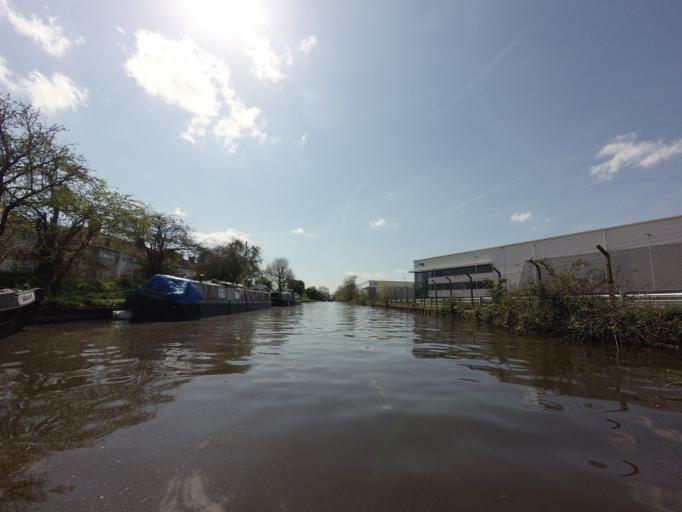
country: GB
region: England
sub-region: Greater London
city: Southall
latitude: 51.5113
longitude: -0.3912
